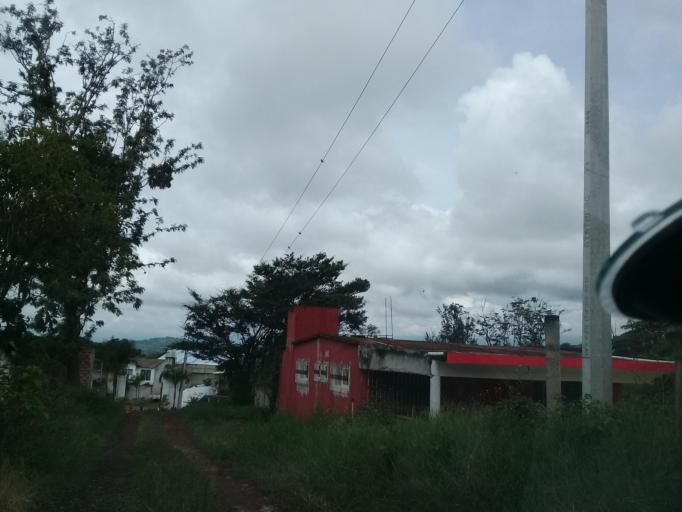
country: MX
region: Veracruz
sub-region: Emiliano Zapata
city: Jacarandas
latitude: 19.4799
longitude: -96.8522
